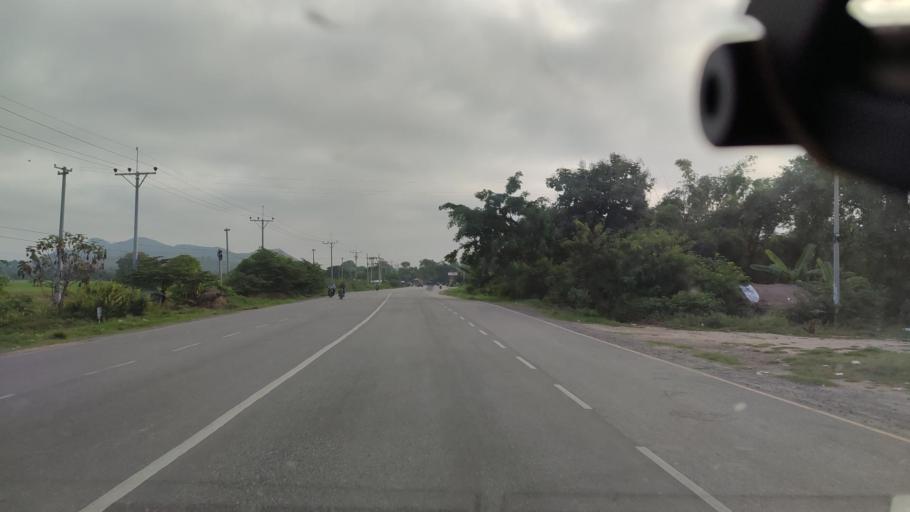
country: MM
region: Mandalay
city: Mandalay
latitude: 22.0749
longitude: 96.1425
